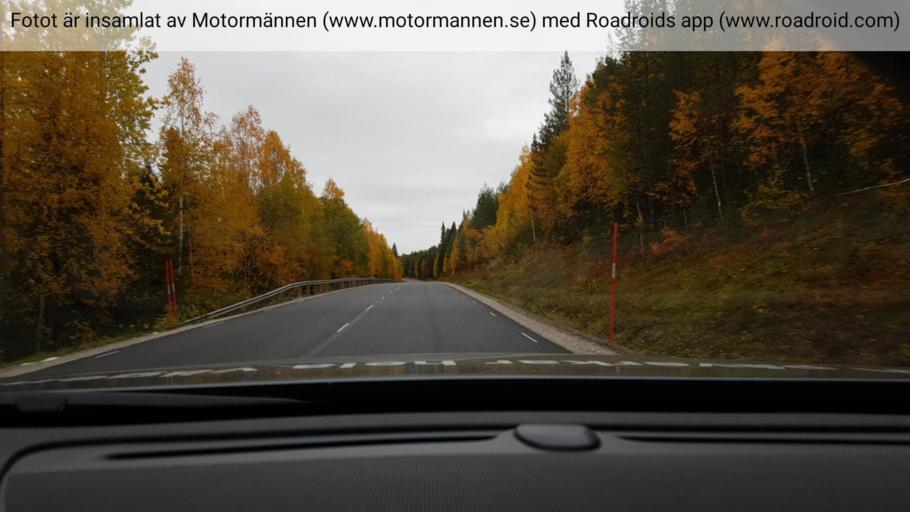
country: SE
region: Norrbotten
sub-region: Overkalix Kommun
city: OEverkalix
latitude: 66.4647
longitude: 22.7929
